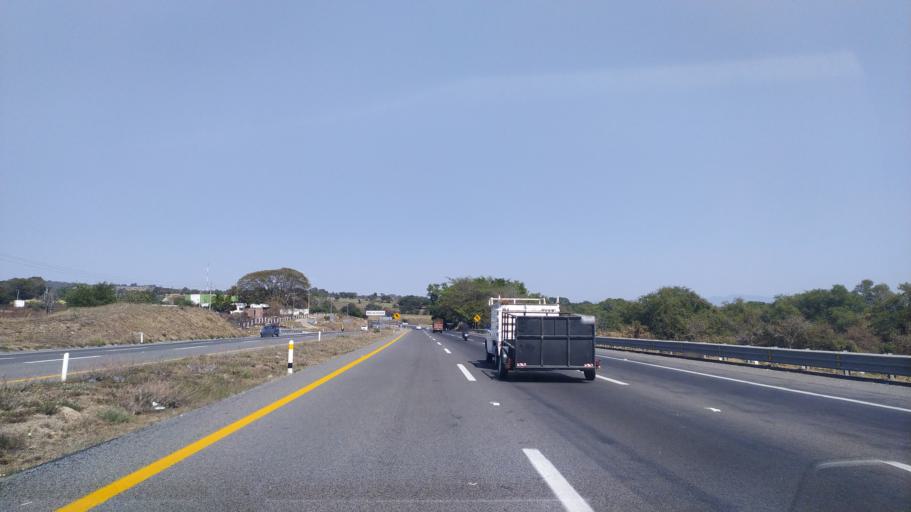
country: MX
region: Colima
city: Cuauhtemoc
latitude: 19.3154
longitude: -103.5968
